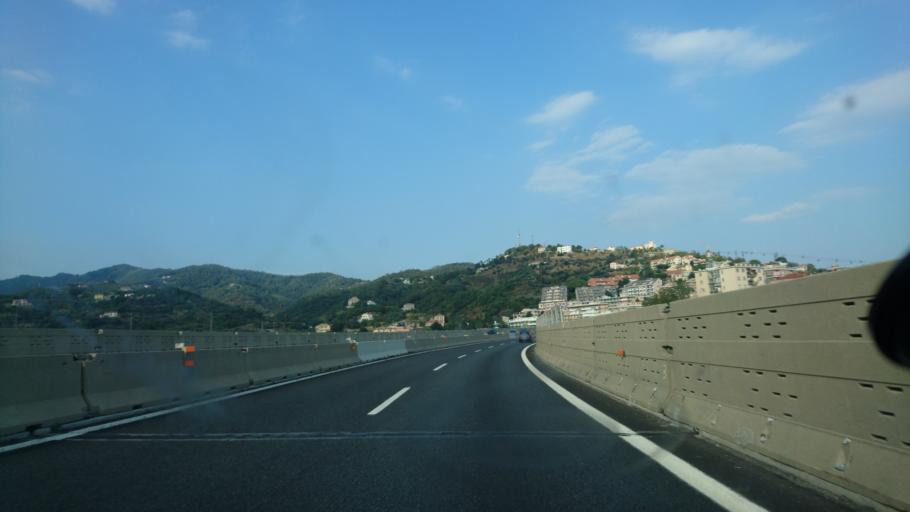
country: IT
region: Liguria
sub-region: Provincia di Savona
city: Savona
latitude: 44.3167
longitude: 8.4705
